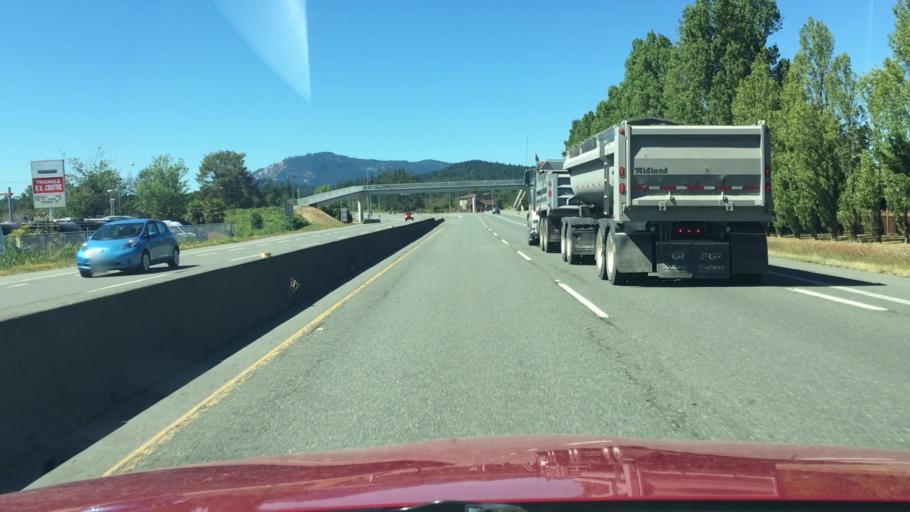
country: CA
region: British Columbia
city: North Saanich
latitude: 48.6604
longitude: -123.4154
